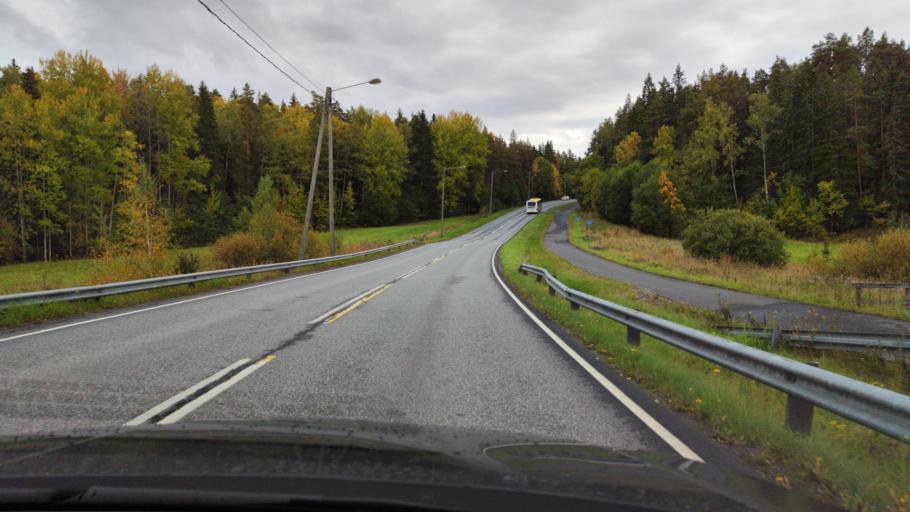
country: FI
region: Varsinais-Suomi
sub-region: Turku
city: Raisio
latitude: 60.3647
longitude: 22.1781
